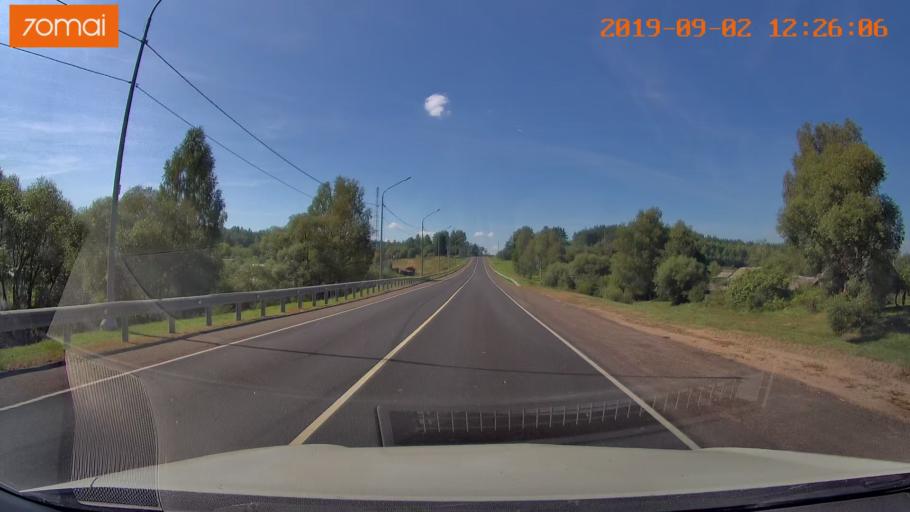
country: RU
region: Smolensk
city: Shumyachi
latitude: 53.8584
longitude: 32.5722
